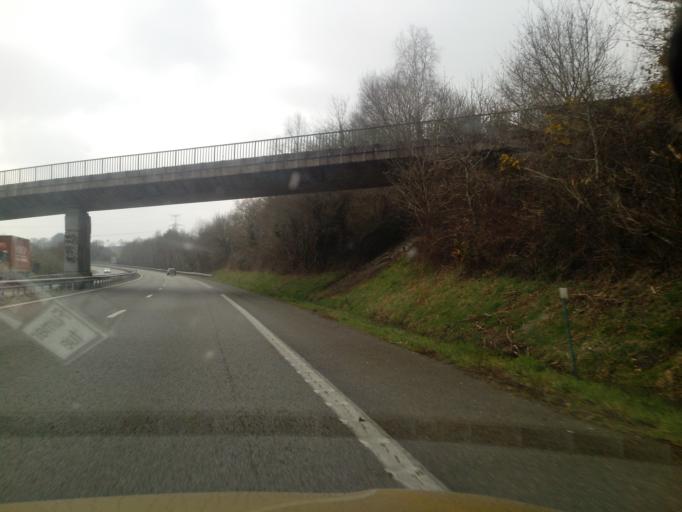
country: FR
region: Brittany
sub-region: Departement du Morbihan
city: Elven
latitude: 47.7475
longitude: -2.5671
